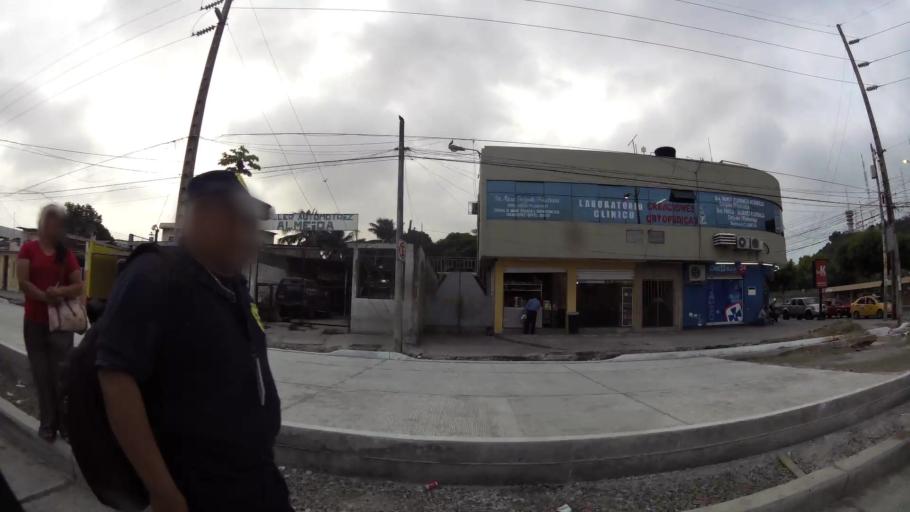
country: EC
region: Guayas
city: Eloy Alfaro
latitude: -2.1754
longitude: -79.8837
